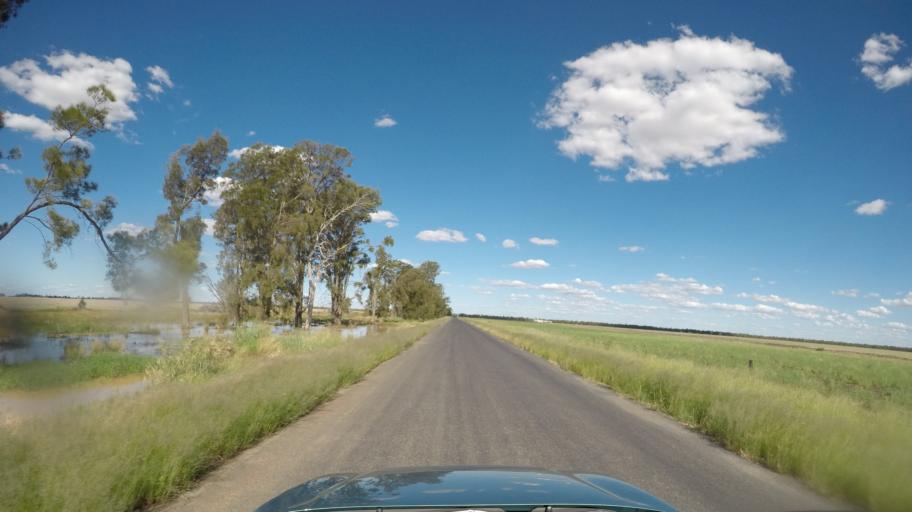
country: AU
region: Queensland
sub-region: Goondiwindi
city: Goondiwindi
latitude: -28.1772
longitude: 150.2665
